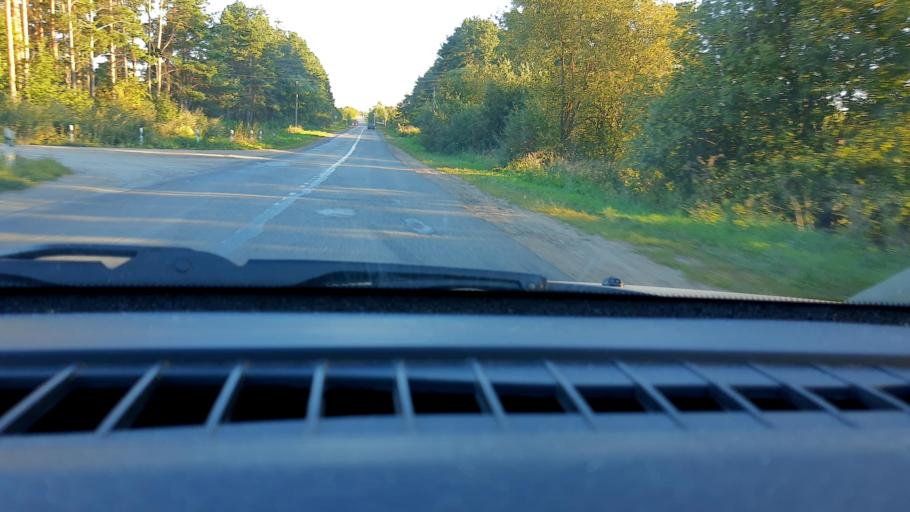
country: RU
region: Nizjnij Novgorod
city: Burevestnik
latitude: 56.1499
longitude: 43.7772
